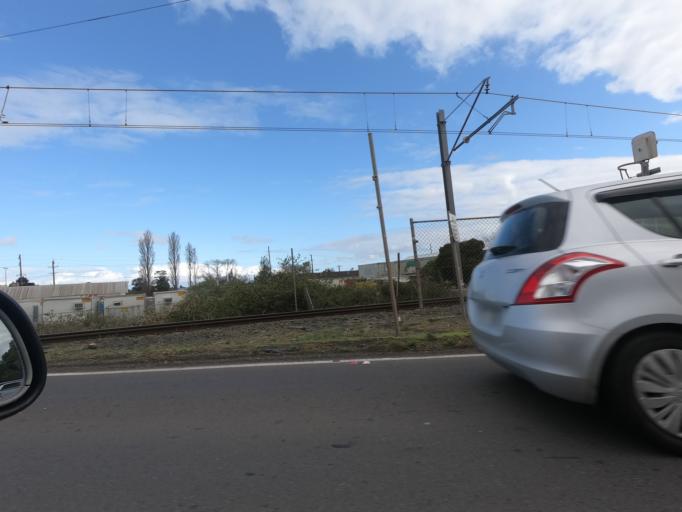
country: AU
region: New South Wales
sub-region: Wollongong
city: Koonawarra
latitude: -34.4706
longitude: 150.8161
